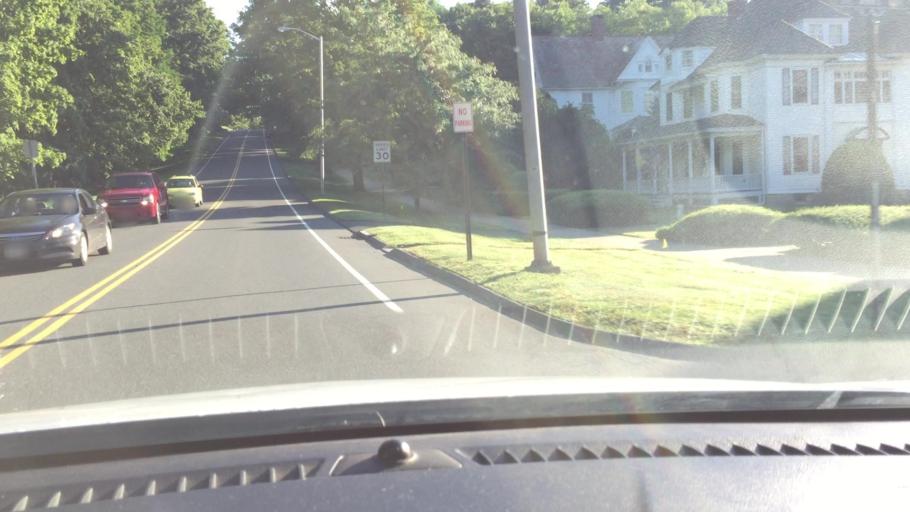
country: US
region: Massachusetts
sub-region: Berkshire County
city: Lenox
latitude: 42.3611
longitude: -73.2831
